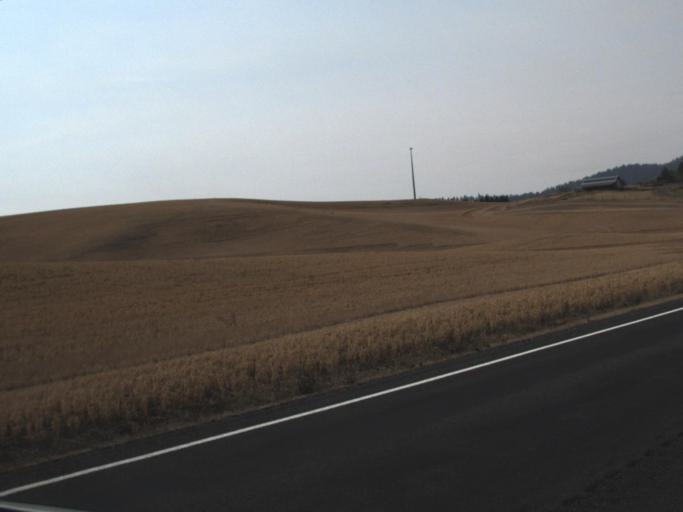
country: US
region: Washington
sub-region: Whitman County
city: Pullman
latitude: 46.8940
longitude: -117.1091
